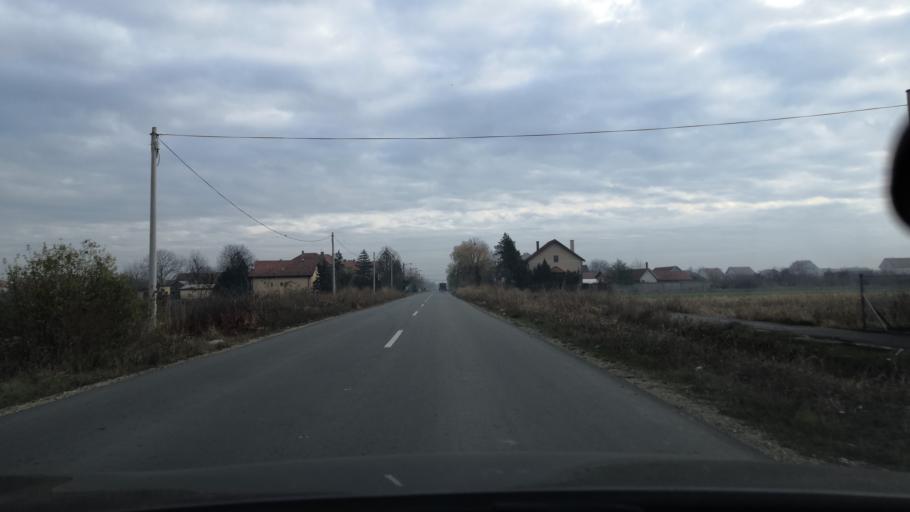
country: RS
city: Ugrinovci
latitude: 44.8799
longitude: 20.1666
